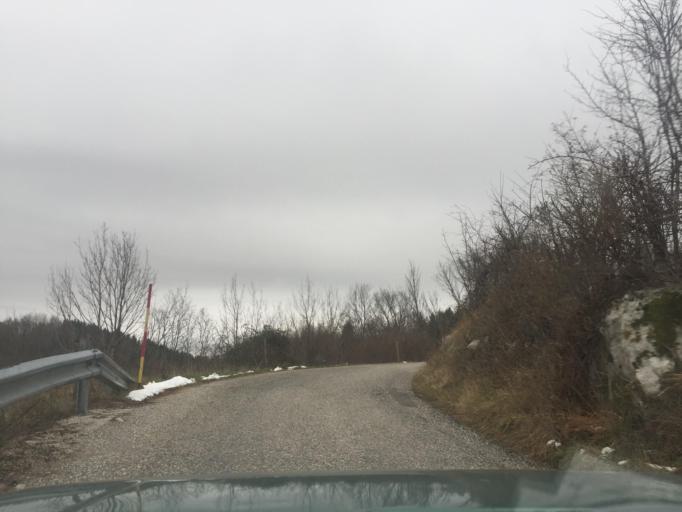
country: SI
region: Kanal
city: Kanal
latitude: 46.0608
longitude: 13.6950
